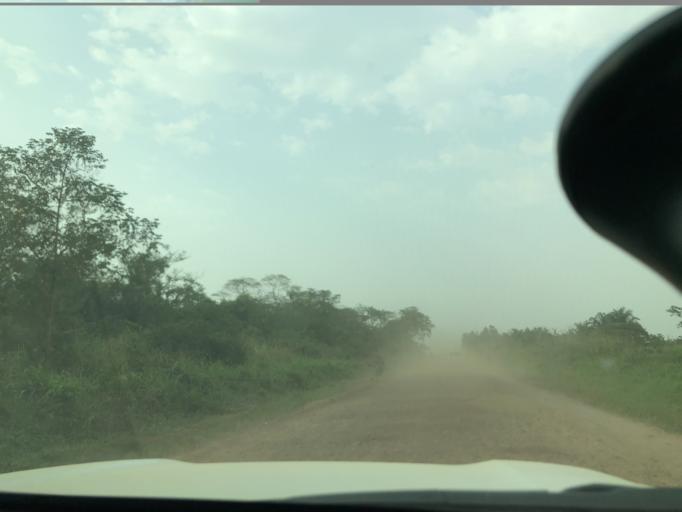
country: UG
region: Western Region
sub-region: Kasese District
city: Margherita
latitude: 0.2545
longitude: 29.6788
